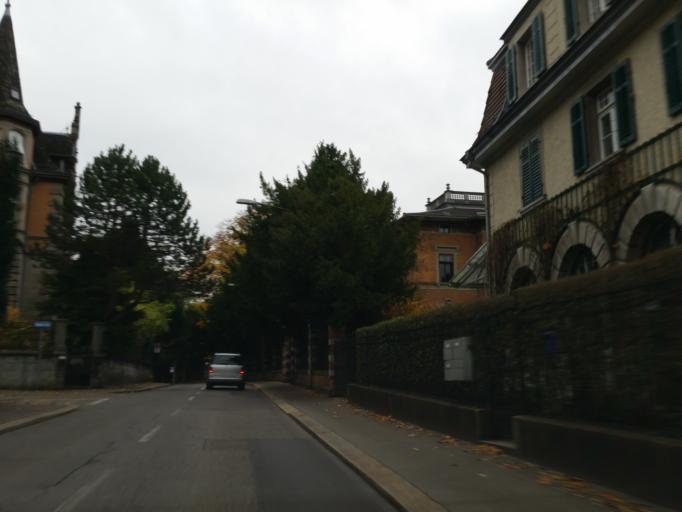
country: CH
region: Zurich
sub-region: Bezirk Zuerich
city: Zuerich (Kreis 8) / Muehlebach
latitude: 47.3628
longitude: 8.5552
